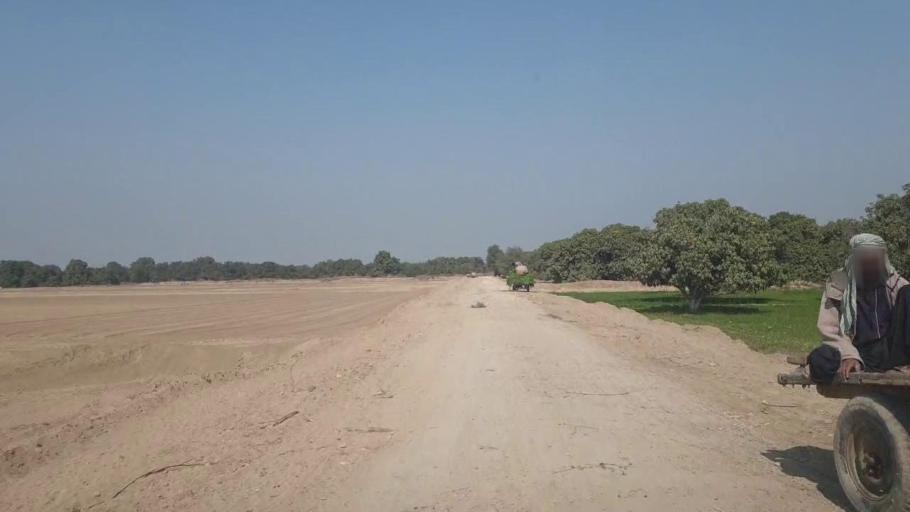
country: PK
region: Sindh
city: Tando Allahyar
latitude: 25.4486
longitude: 68.8328
